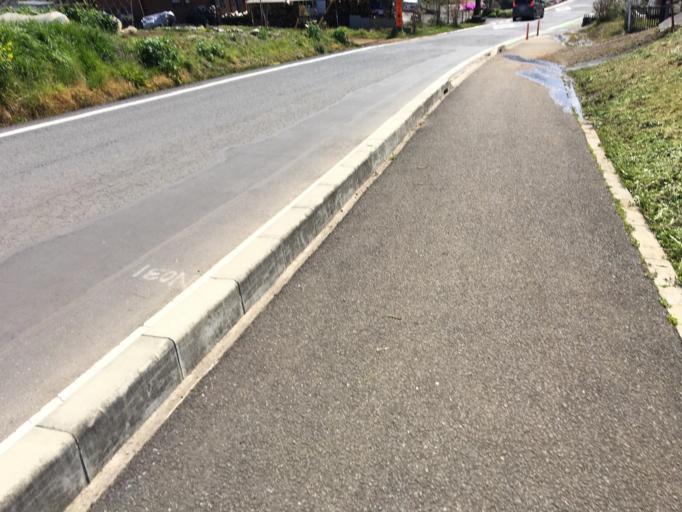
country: JP
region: Saitama
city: Sayama
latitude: 35.8965
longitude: 139.3666
